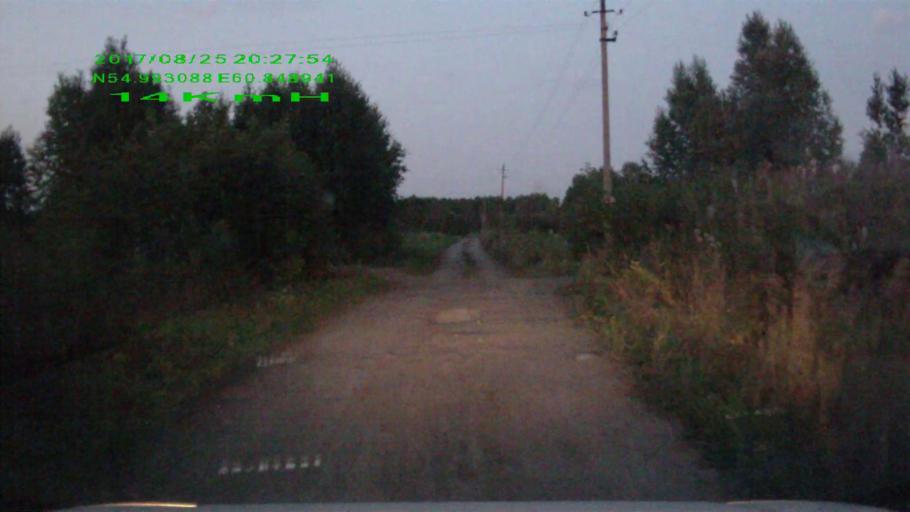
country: RU
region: Chelyabinsk
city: Timiryazevskiy
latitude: 54.9931
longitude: 60.8489
